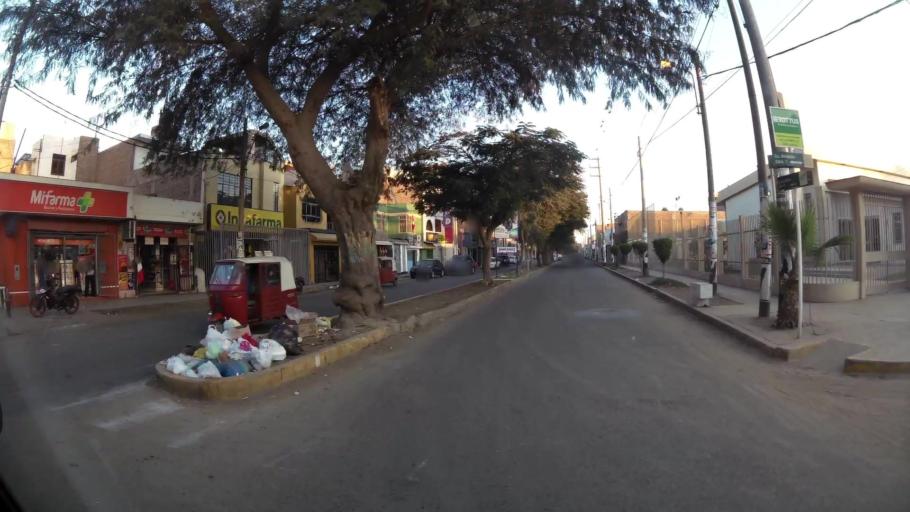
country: PE
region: Ica
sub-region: Provincia de Ica
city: Ica
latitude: -14.0772
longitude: -75.7266
